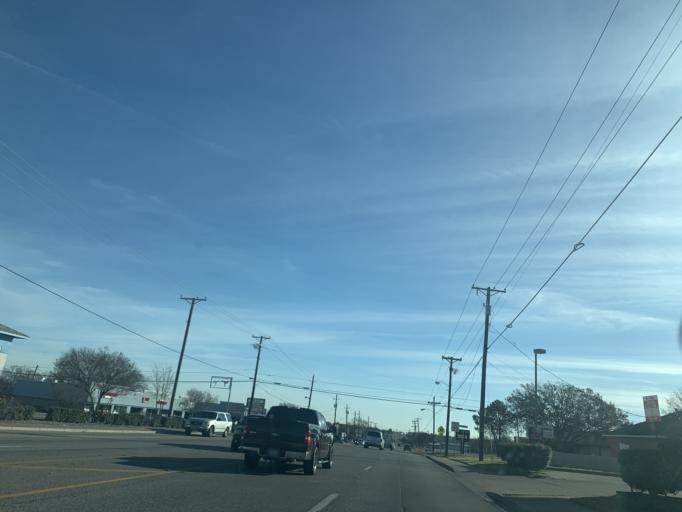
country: US
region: Texas
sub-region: Dallas County
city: DeSoto
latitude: 32.5896
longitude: -96.8566
